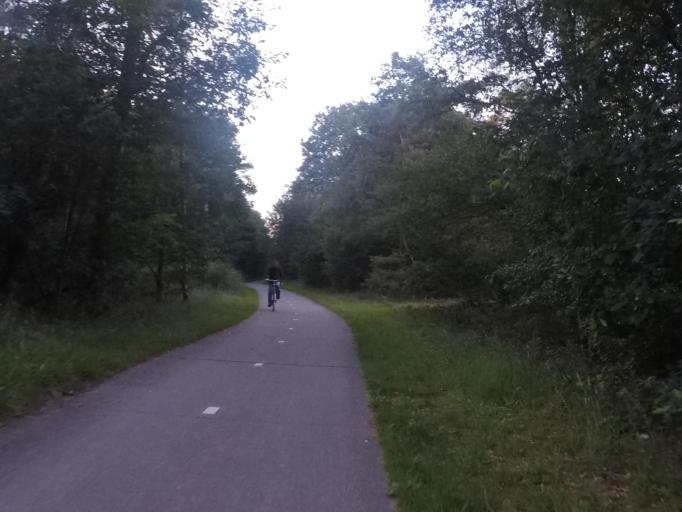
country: NL
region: Drenthe
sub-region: Gemeente Westerveld
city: Dwingeloo
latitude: 52.8715
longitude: 6.3210
